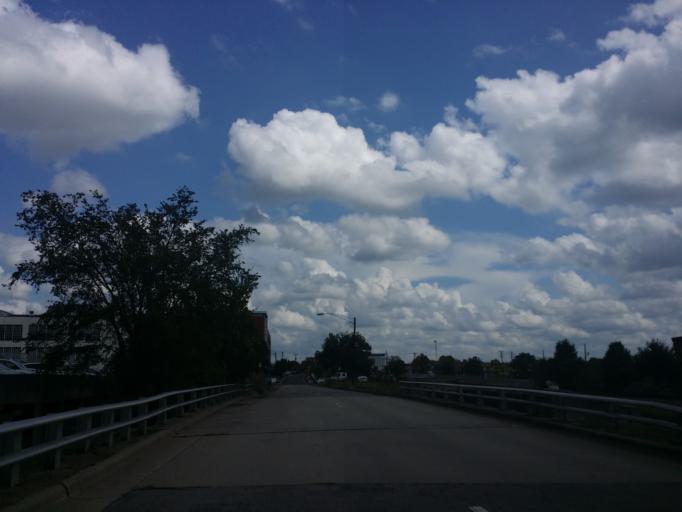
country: US
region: North Carolina
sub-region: Durham County
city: Durham
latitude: 35.9932
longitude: -78.8993
